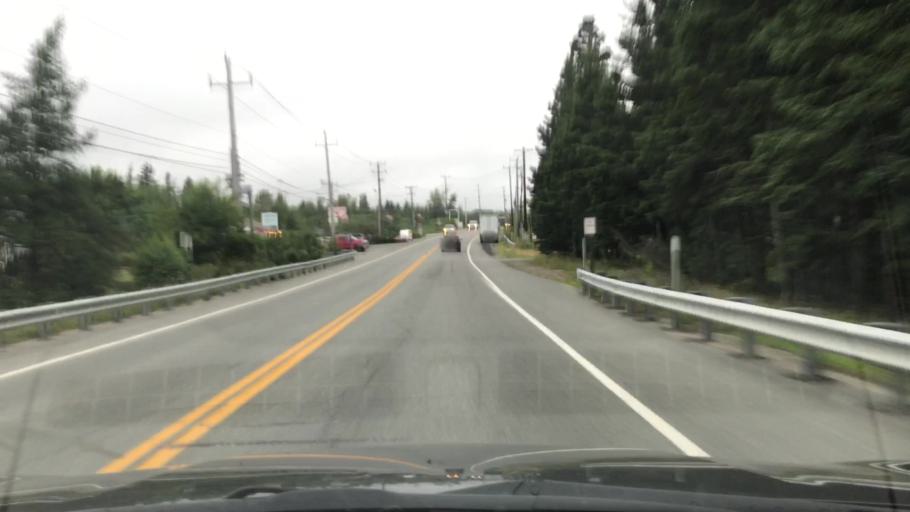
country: US
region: Maine
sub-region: Hancock County
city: Trenton
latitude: 44.4316
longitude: -68.3681
